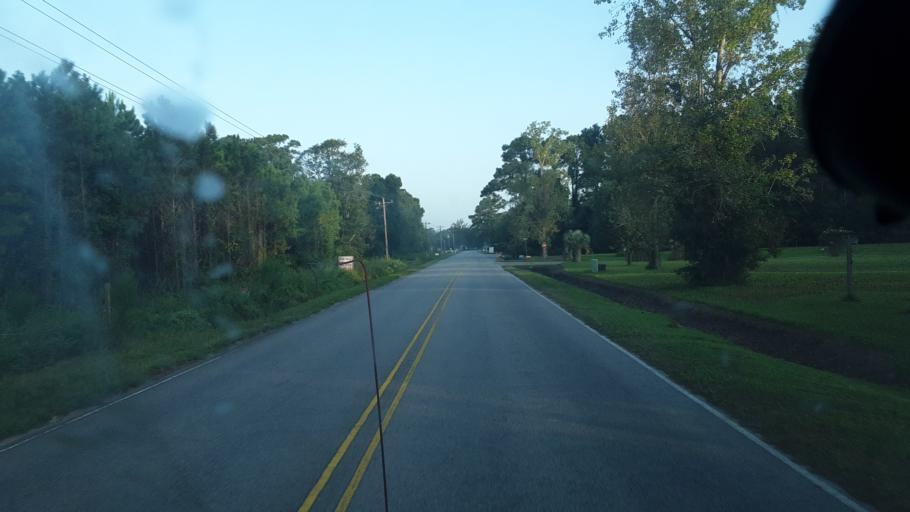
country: US
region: North Carolina
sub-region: Brunswick County
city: Calabash
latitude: 33.8804
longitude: -78.5443
